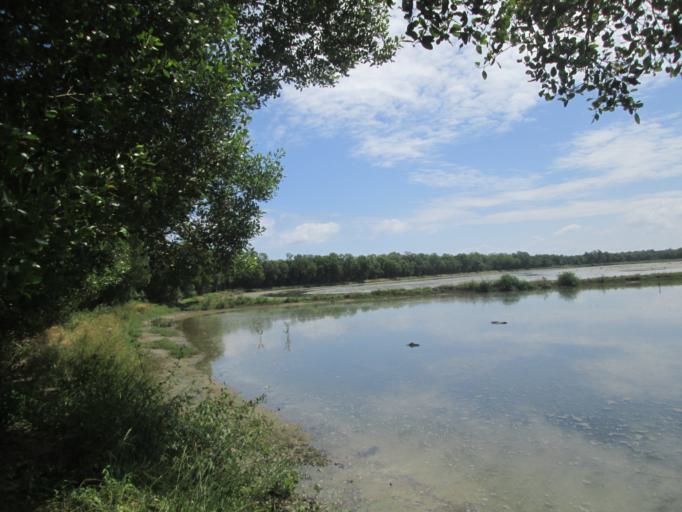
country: PH
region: Ilocos
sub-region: Province of Pangasinan
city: Pangapisan
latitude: 16.2471
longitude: 119.9256
